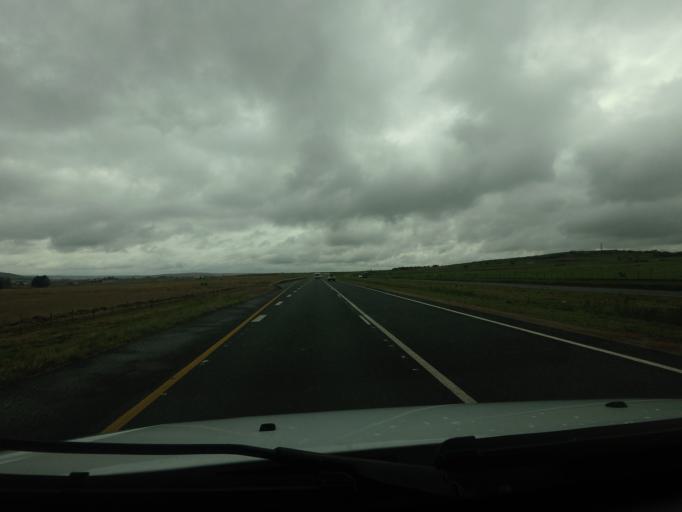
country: ZA
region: Gauteng
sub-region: City of Tshwane Metropolitan Municipality
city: Bronkhorstspruit
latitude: -25.8732
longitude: 28.9643
